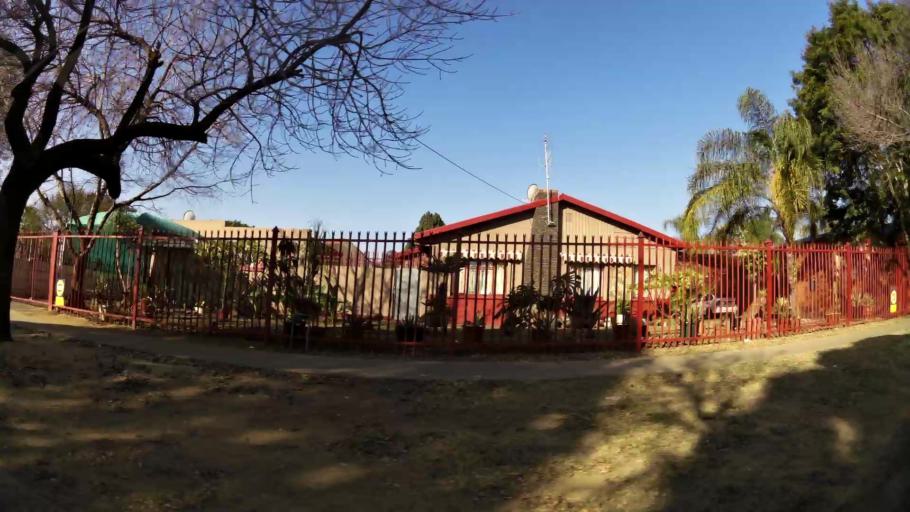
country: ZA
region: Gauteng
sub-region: City of Tshwane Metropolitan Municipality
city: Pretoria
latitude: -25.7220
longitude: 28.1519
